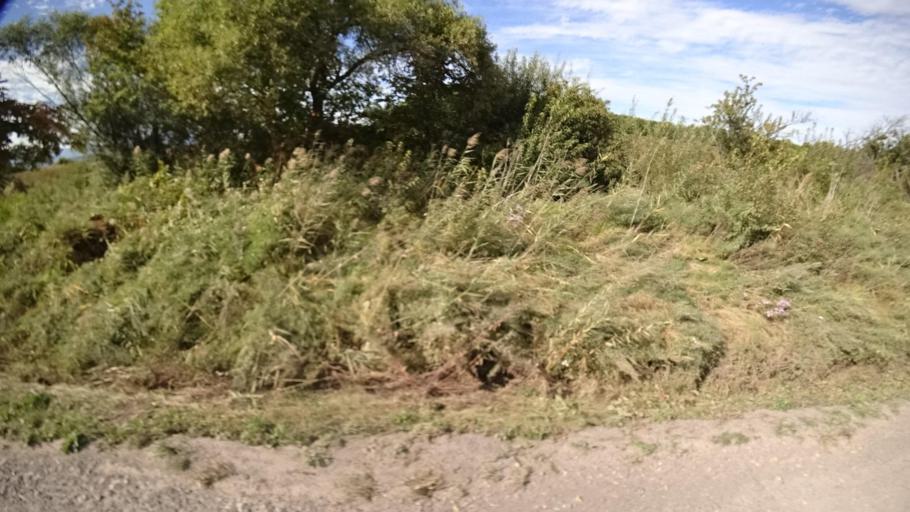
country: RU
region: Primorskiy
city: Yakovlevka
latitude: 44.3888
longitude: 133.5440
